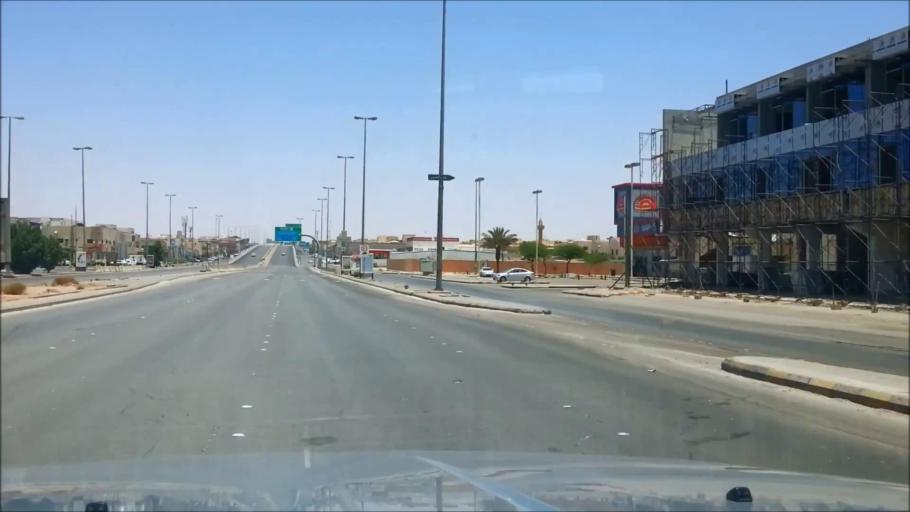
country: SA
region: Ar Riyad
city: Riyadh
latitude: 24.7579
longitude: 46.6746
